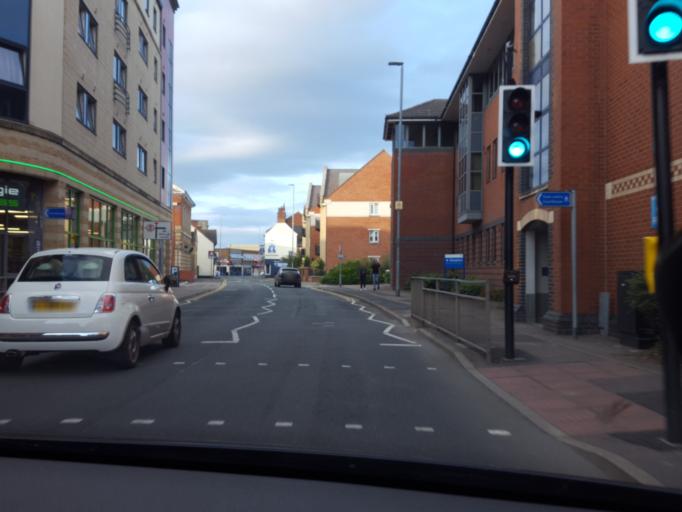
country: GB
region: England
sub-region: Leicestershire
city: Loughborough
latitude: 52.7695
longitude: -1.2056
